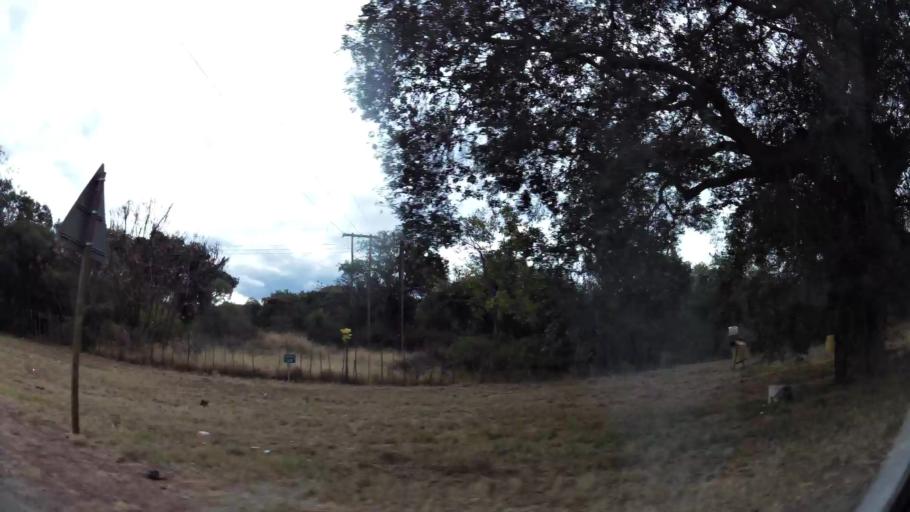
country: ZA
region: Limpopo
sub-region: Waterberg District Municipality
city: Modimolle
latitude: -24.6735
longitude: 28.4479
